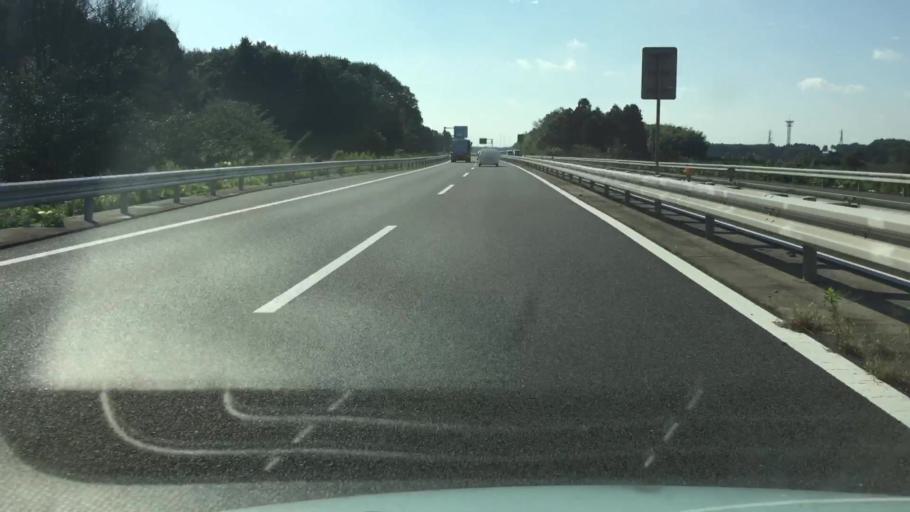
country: JP
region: Tochigi
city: Mooka
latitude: 36.4983
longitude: 139.9898
